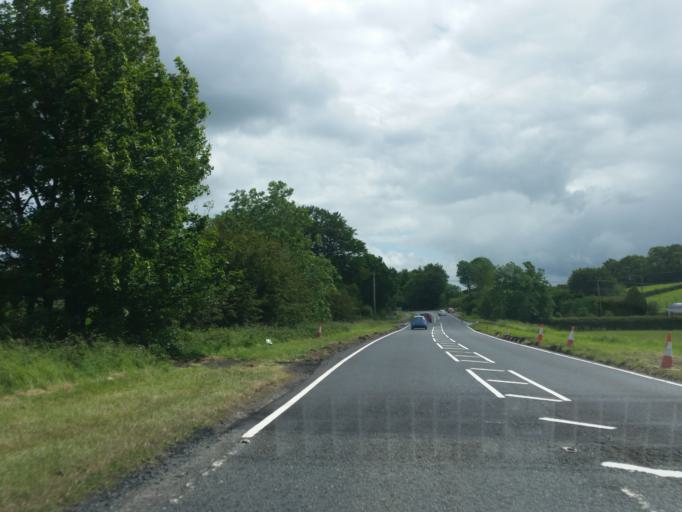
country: IE
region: Ulster
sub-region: County Monaghan
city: Monaghan
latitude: 54.4692
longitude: -7.0481
